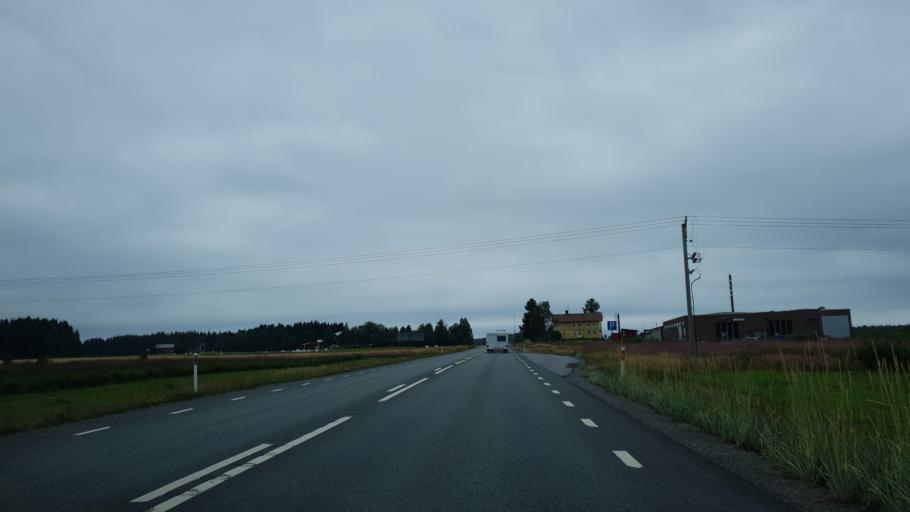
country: SE
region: Vaesterbotten
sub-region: Skelleftea Kommun
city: Burea
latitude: 64.3756
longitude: 21.3036
